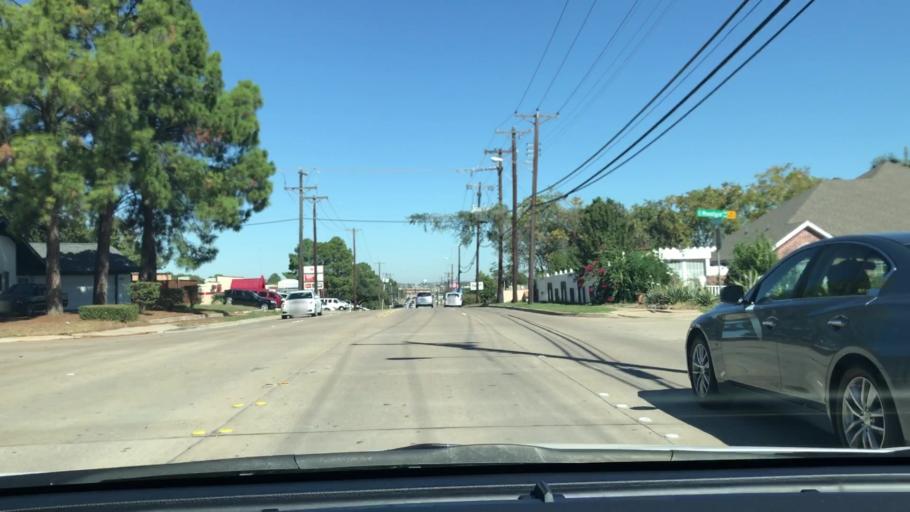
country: US
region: Texas
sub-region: Tarrant County
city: Hurst
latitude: 32.8310
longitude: -97.1864
